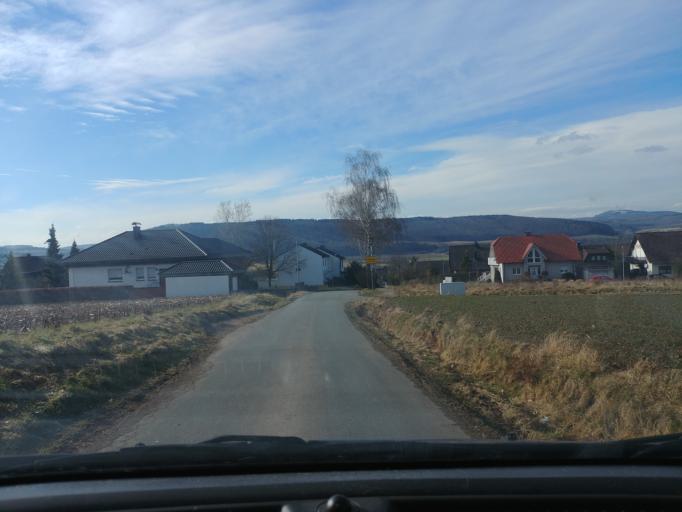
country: DE
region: Lower Saxony
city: Holzminden
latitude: 51.7929
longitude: 9.4391
